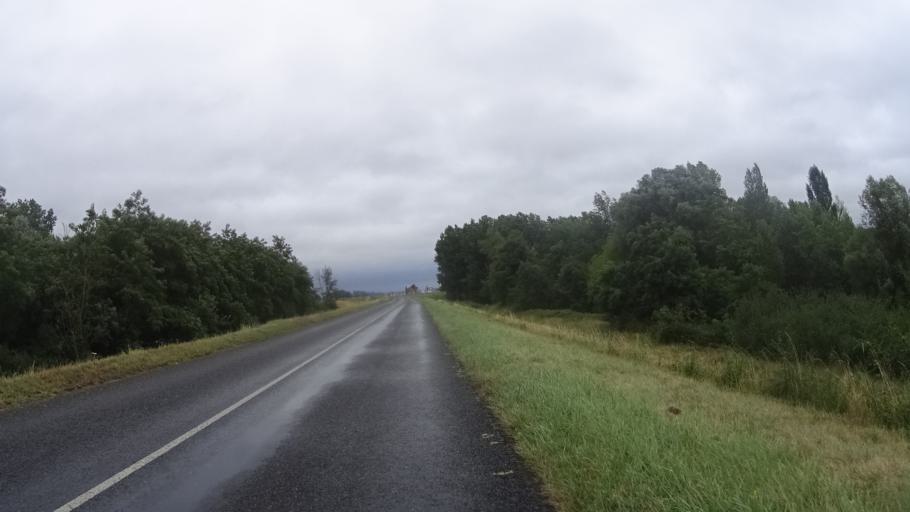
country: FR
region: Centre
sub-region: Departement du Loir-et-Cher
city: Chouzy-sur-Cisse
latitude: 47.5325
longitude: 1.2781
